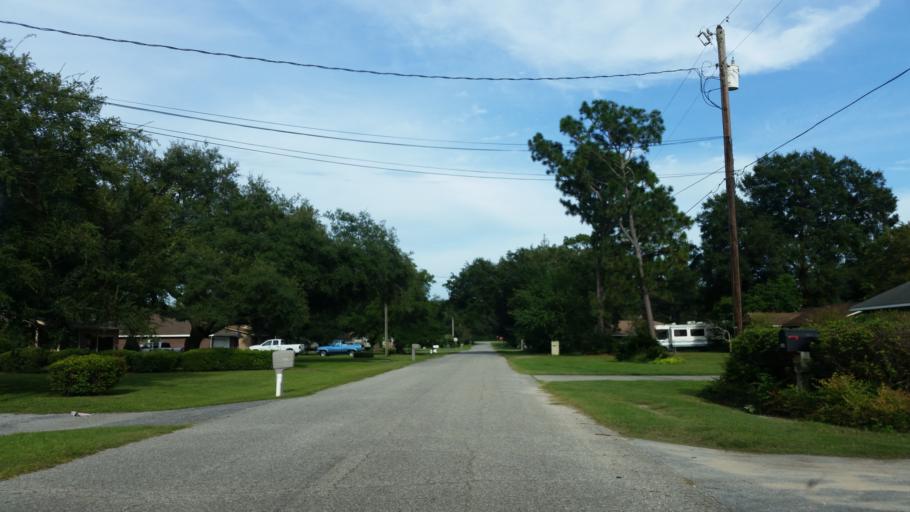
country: US
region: Florida
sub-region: Escambia County
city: Ferry Pass
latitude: 30.5073
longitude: -87.1936
